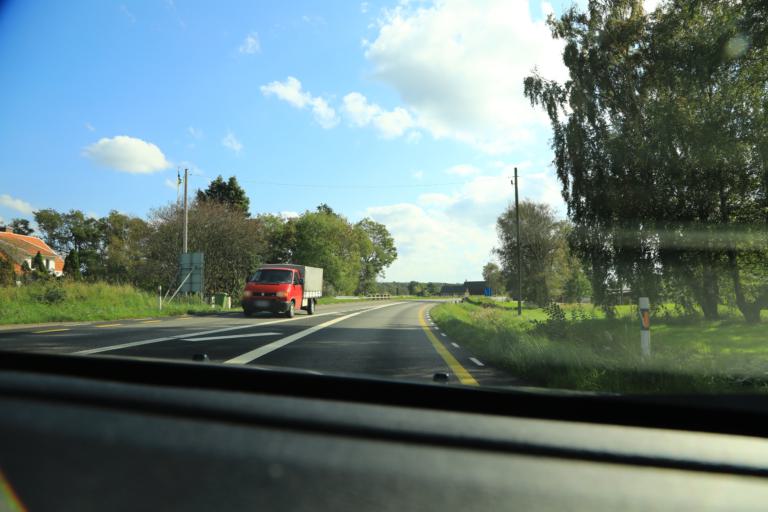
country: SE
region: Halland
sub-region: Varbergs Kommun
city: Tvaaker
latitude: 57.0117
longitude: 12.3571
